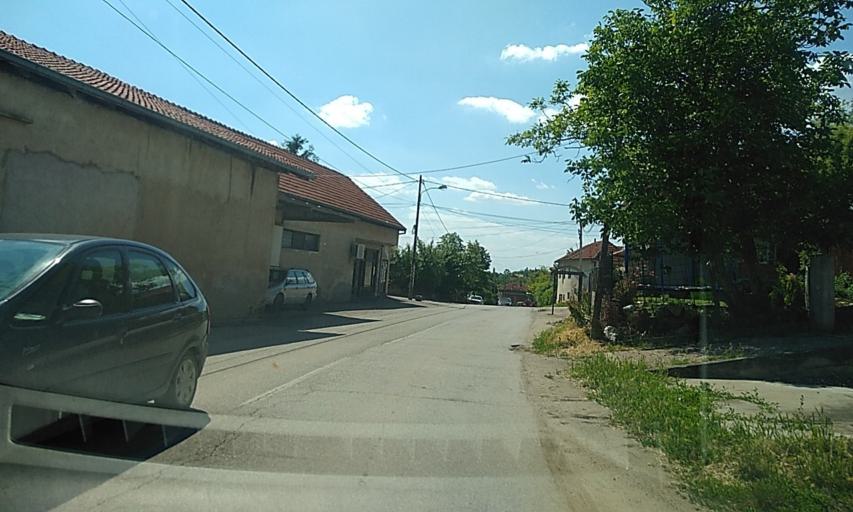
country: RS
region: Central Serbia
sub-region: Nisavski Okrug
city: Niska Banja
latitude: 43.3639
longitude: 21.9708
